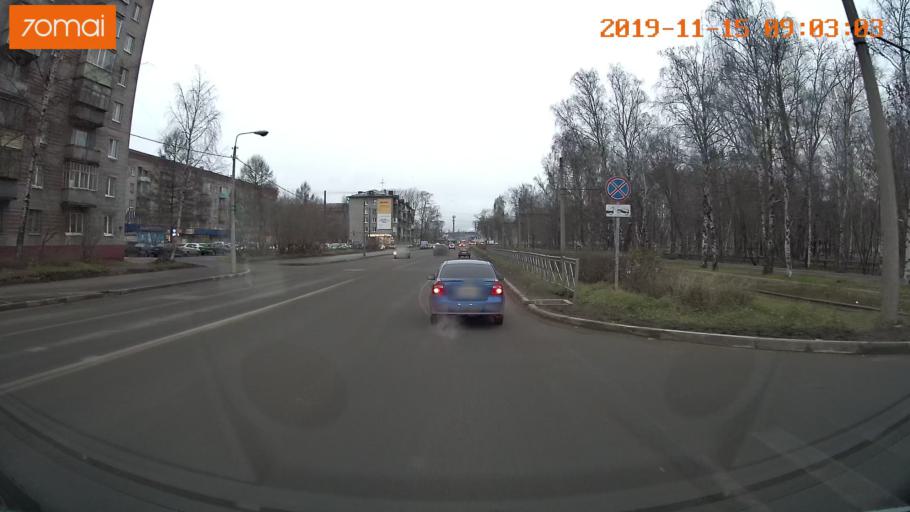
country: RU
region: Vologda
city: Cherepovets
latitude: 59.1373
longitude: 37.9249
